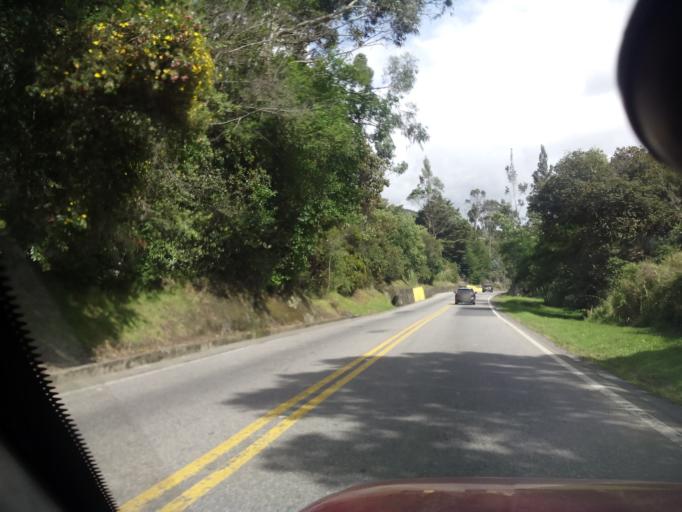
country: CO
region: Boyaca
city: Arcabuco
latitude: 5.7312
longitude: -73.4013
